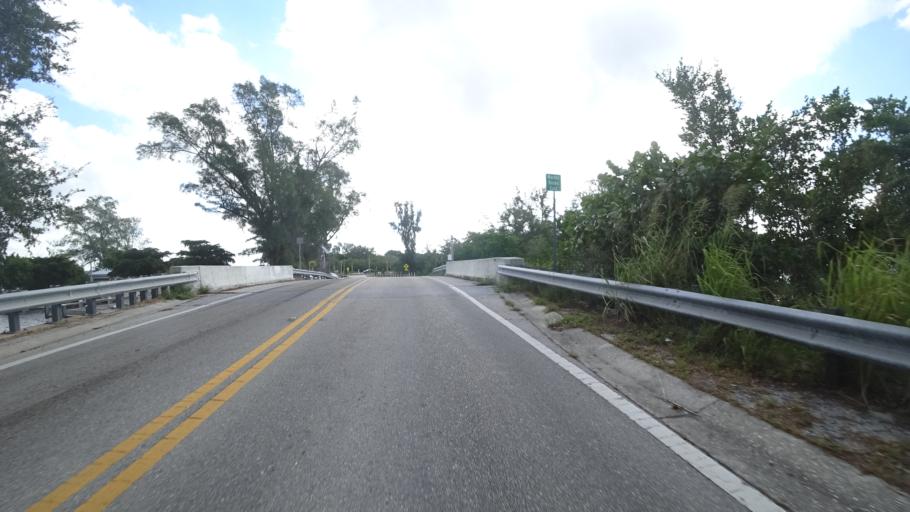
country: US
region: Florida
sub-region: Manatee County
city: West Bradenton
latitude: 27.5096
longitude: -82.6189
